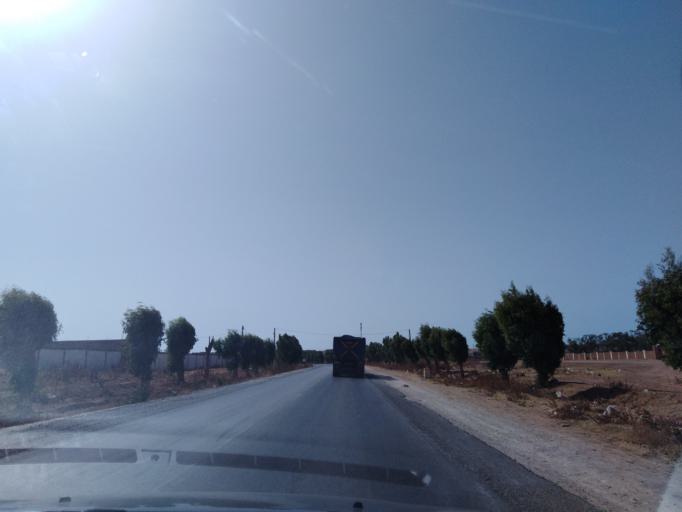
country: MA
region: Doukkala-Abda
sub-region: Safi
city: Safi
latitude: 32.2517
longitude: -8.9744
